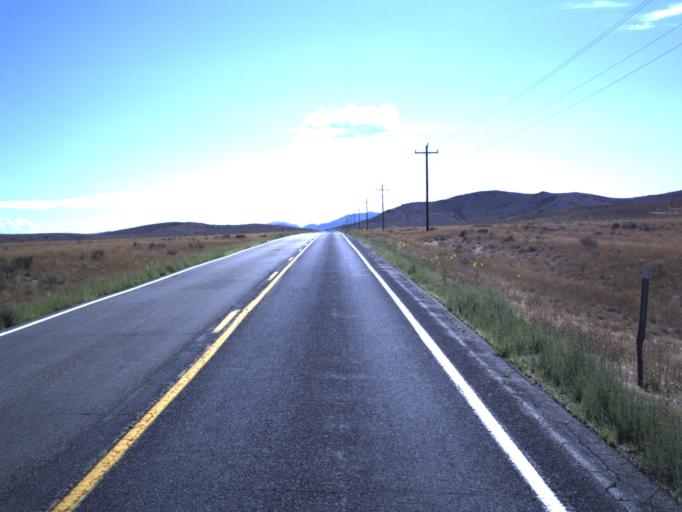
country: US
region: Utah
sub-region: Utah County
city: Eagle Mountain
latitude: 40.0808
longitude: -112.4056
